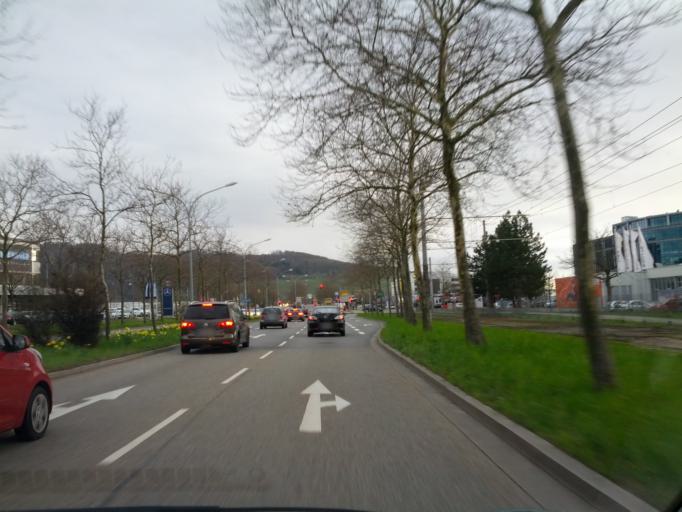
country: DE
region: Baden-Wuerttemberg
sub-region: Freiburg Region
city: Ebringen
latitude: 47.9903
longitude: 7.7972
